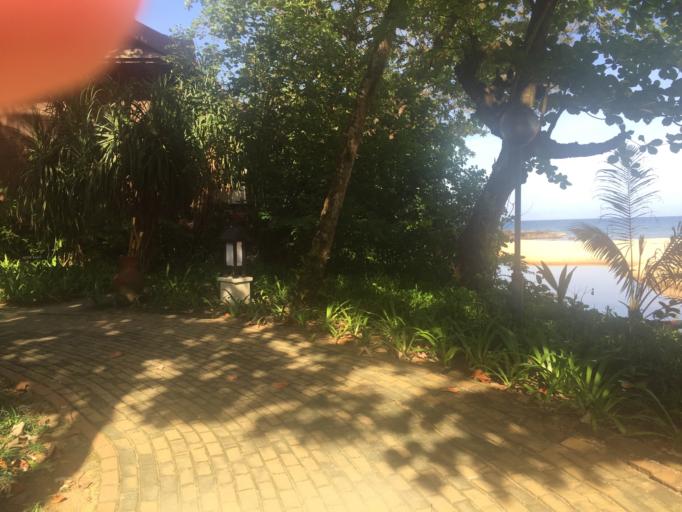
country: MY
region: Terengganu
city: Paka
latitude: 4.8124
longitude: 103.4240
